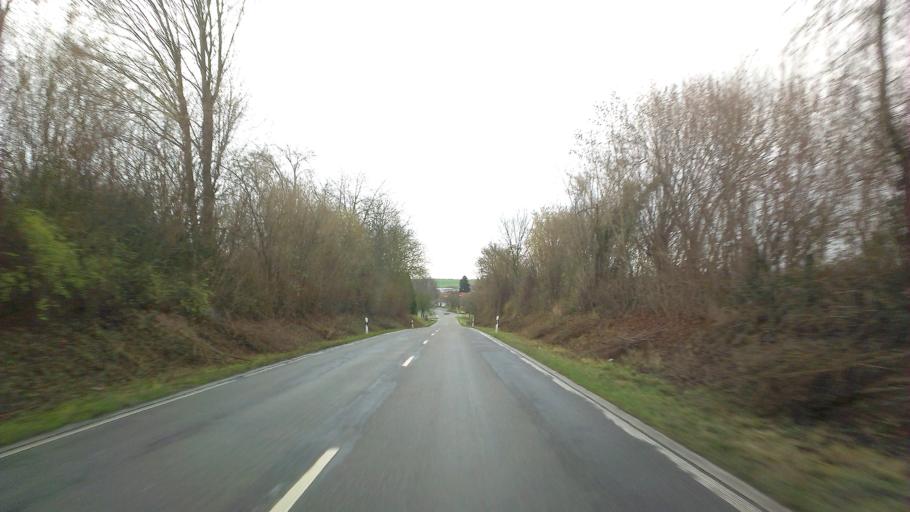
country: DE
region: Baden-Wuerttemberg
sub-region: Karlsruhe Region
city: Kurnbach
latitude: 49.0706
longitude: 8.8497
